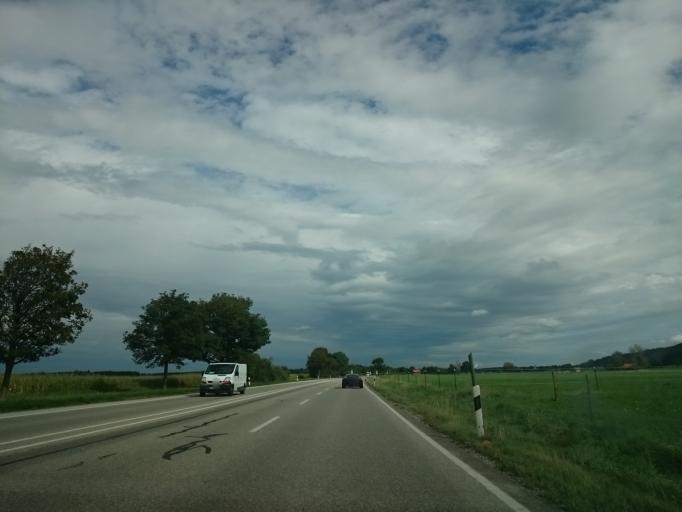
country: DE
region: Bavaria
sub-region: Swabia
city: Rieden
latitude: 47.9401
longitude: 10.6652
